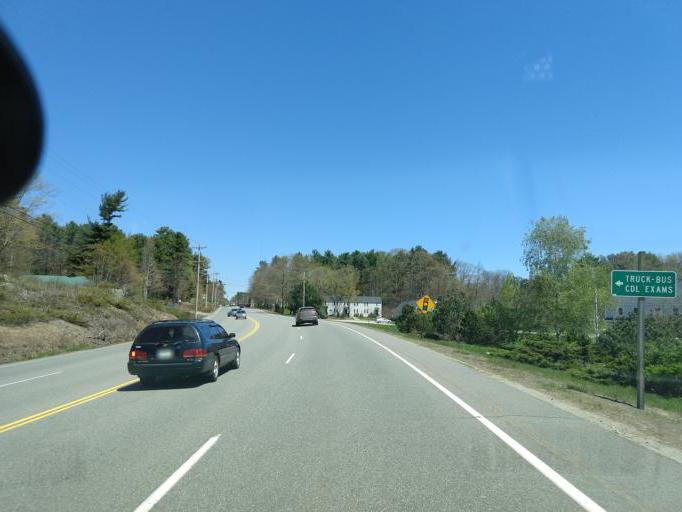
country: US
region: Maine
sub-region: York County
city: York Harbor
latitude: 43.1652
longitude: -70.6427
